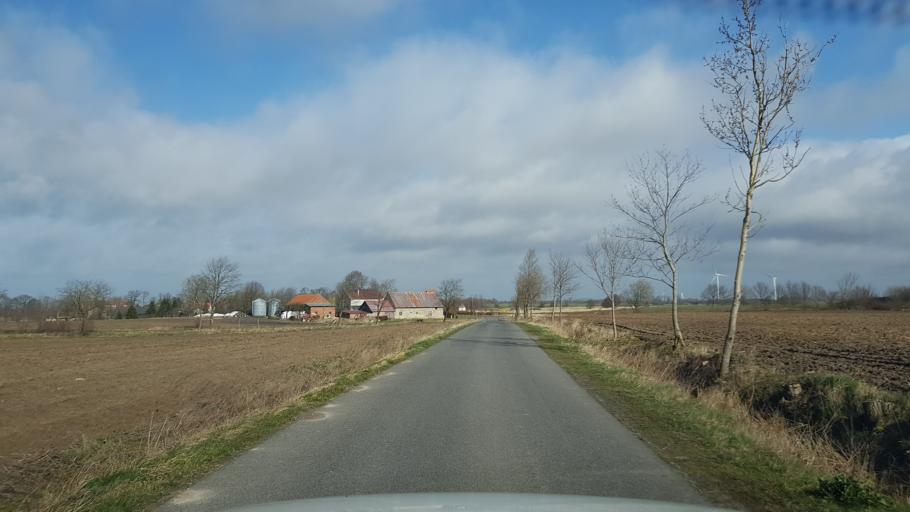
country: PL
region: West Pomeranian Voivodeship
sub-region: Powiat slawienski
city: Slawno
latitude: 54.5077
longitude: 16.6530
